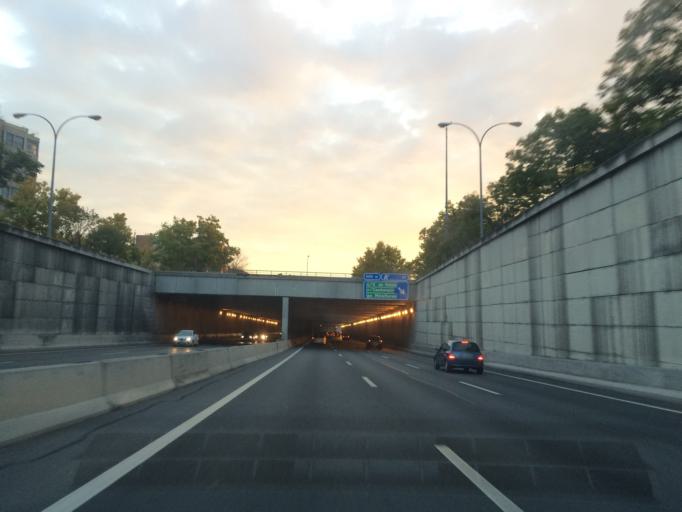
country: ES
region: Madrid
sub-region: Provincia de Madrid
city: Tetuan de las Victorias
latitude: 40.4769
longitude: -3.7198
